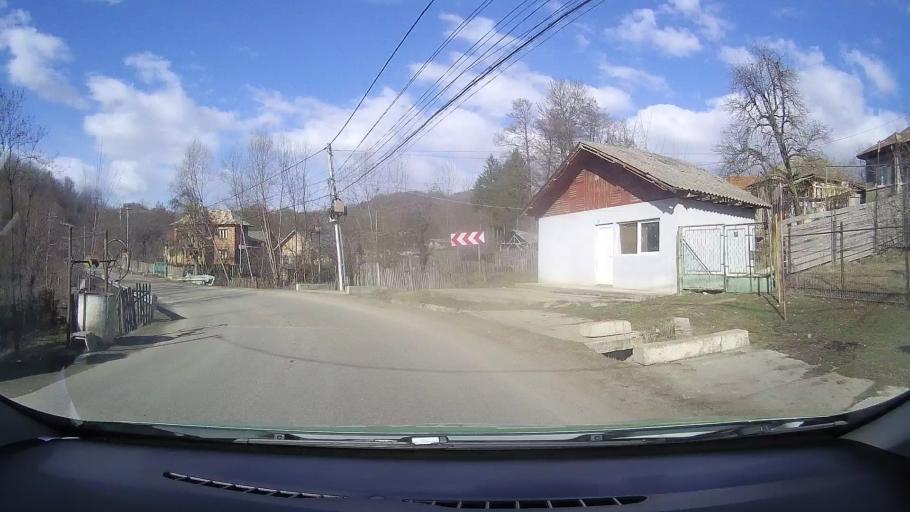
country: RO
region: Dambovita
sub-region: Comuna Varfuri
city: Varfuri
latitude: 45.0900
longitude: 25.4933
